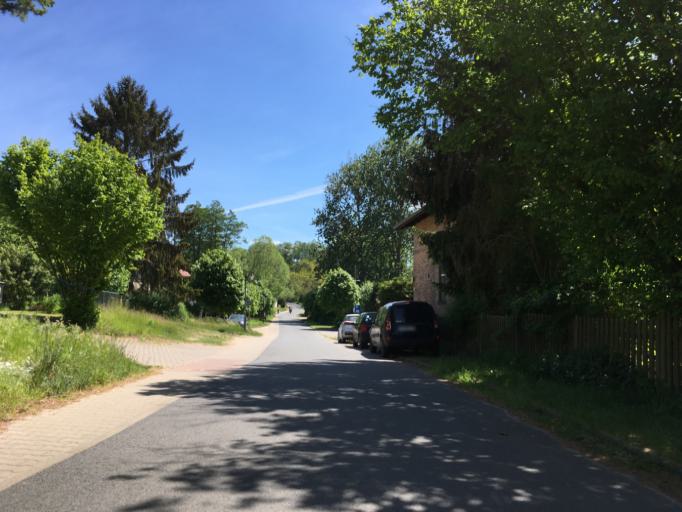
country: DE
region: Brandenburg
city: Niederfinow
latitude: 52.8403
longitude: 13.9026
